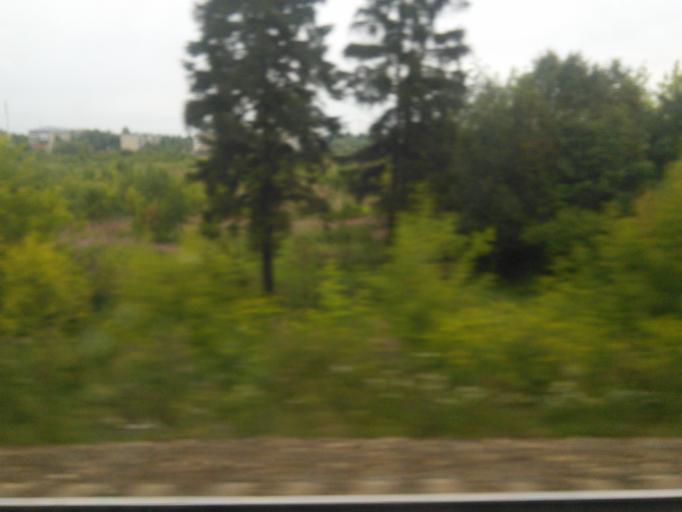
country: RU
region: Moskovskaya
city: Mozhaysk
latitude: 55.4945
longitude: 36.0684
